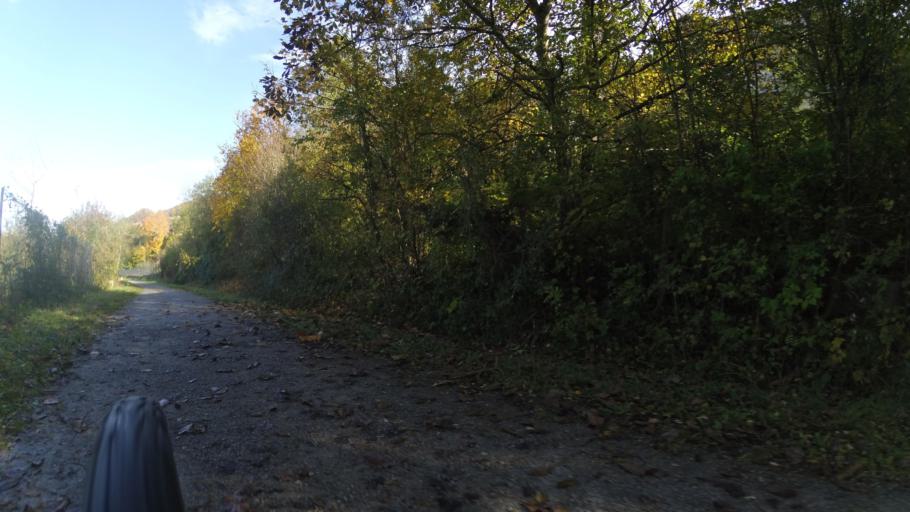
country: DE
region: Baden-Wuerttemberg
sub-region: Regierungsbezirk Stuttgart
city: Niedernhall
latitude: 49.2912
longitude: 9.6160
